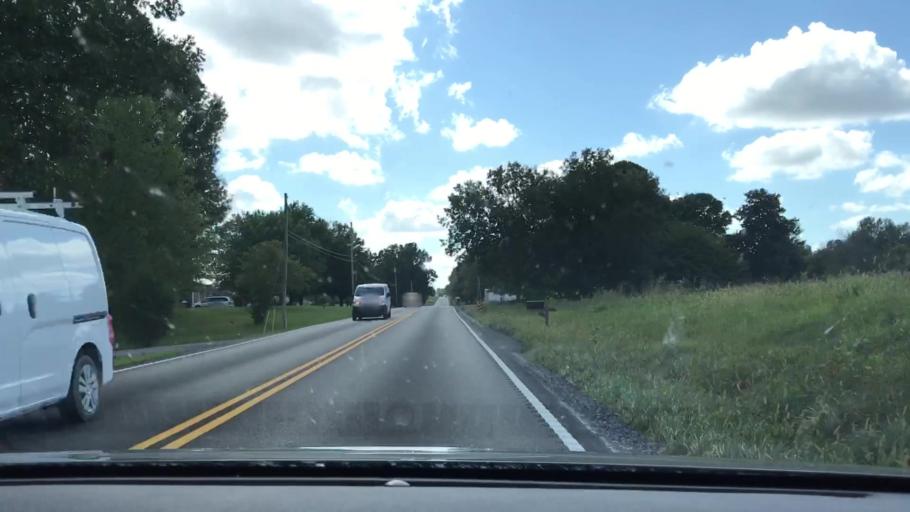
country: US
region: Kentucky
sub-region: Graves County
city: Mayfield
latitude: 36.7715
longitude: -88.5960
